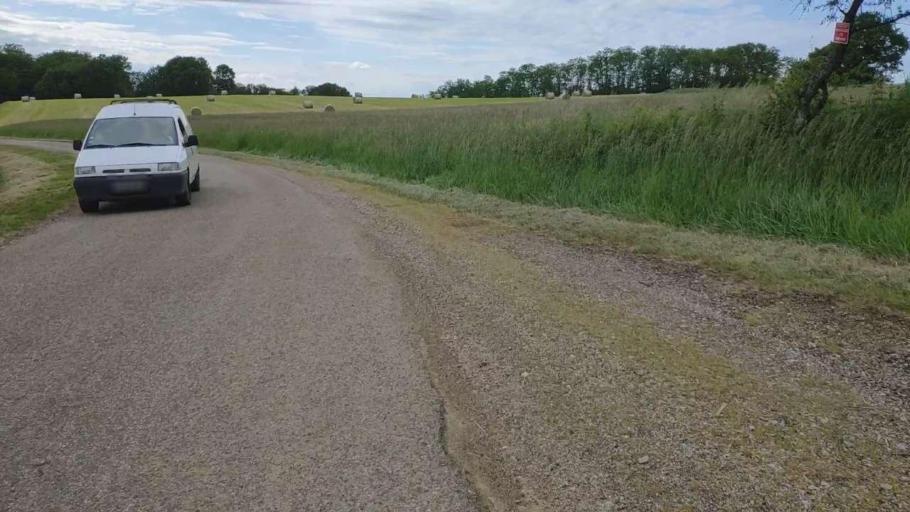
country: FR
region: Franche-Comte
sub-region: Departement du Jura
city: Bletterans
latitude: 46.7998
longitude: 5.5503
